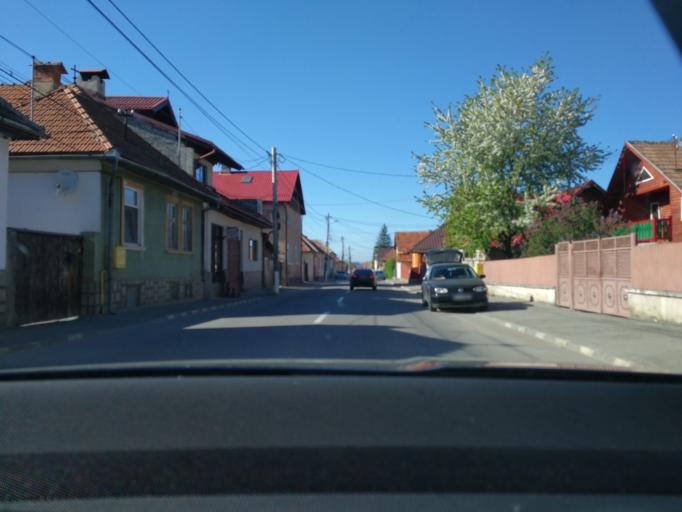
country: RO
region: Brasov
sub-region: Oras Rasnov
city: Rasnov
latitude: 45.5838
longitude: 25.4594
